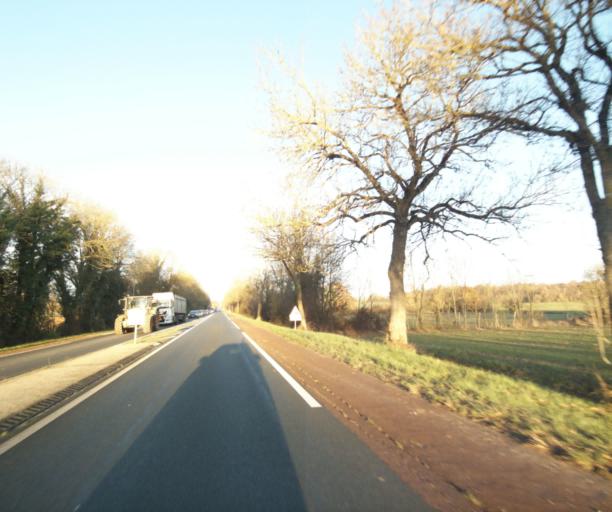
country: FR
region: Poitou-Charentes
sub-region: Departement de la Charente-Maritime
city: Saint-Georges-des-Coteaux
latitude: 45.7790
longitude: -0.7031
